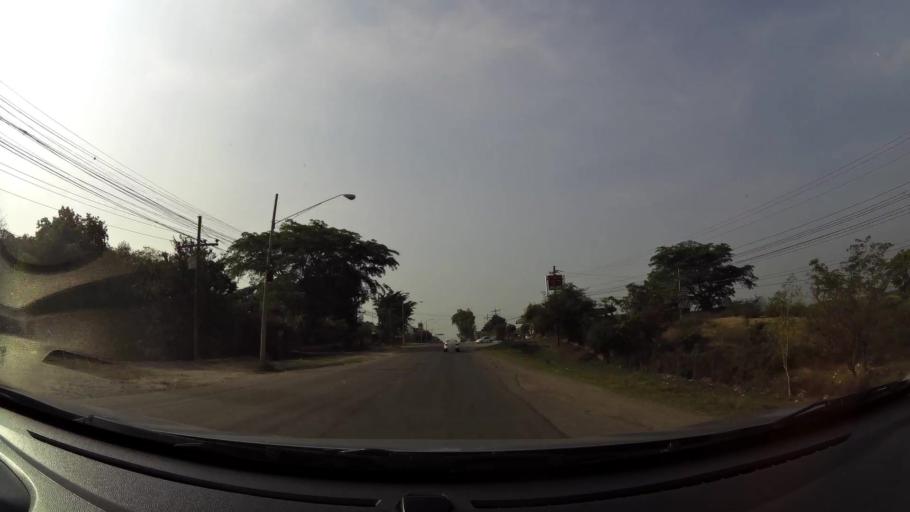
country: HN
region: Comayagua
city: Comayagua
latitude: 14.4428
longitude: -87.6365
